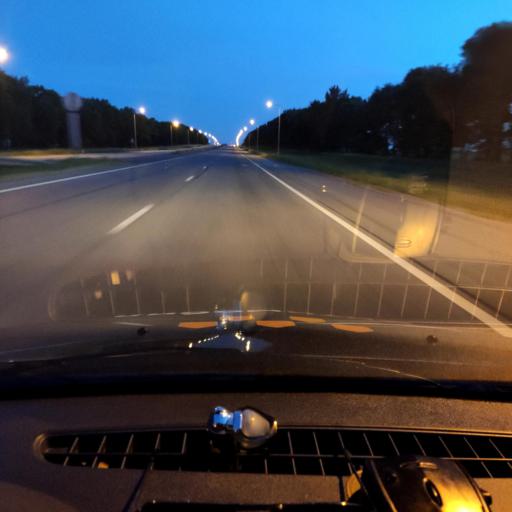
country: RU
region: Belgorod
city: Gubkin
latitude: 51.2489
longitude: 37.5224
